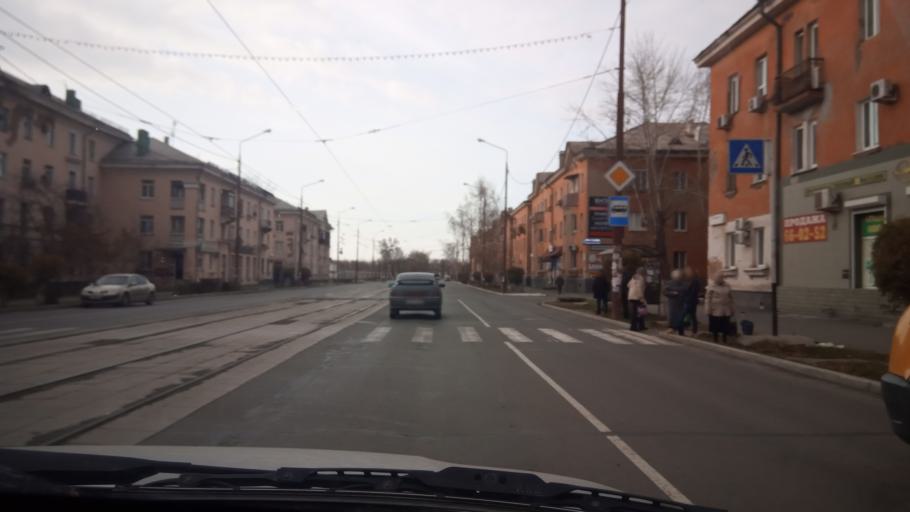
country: RU
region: Orenburg
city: Novotroitsk
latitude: 51.1977
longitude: 58.3319
